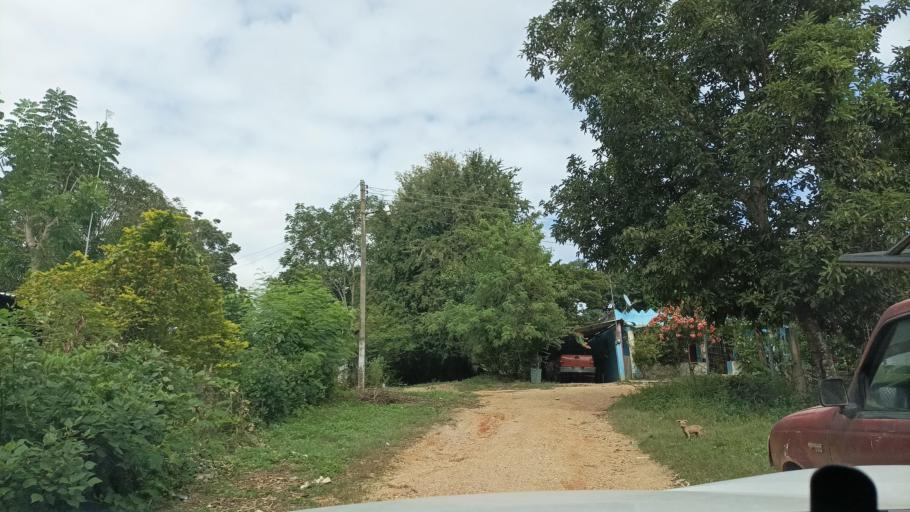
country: MX
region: Veracruz
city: Soconusco
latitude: 17.9612
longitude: -94.8159
